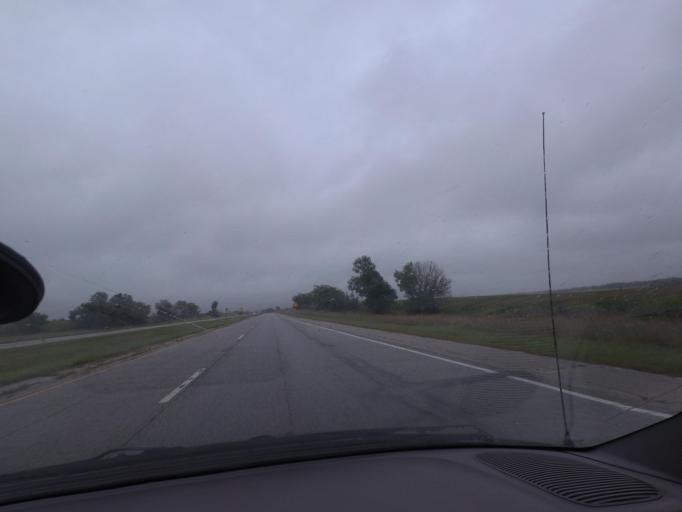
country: US
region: Illinois
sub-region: Pike County
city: Pittsfield
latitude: 39.6707
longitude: -90.8321
